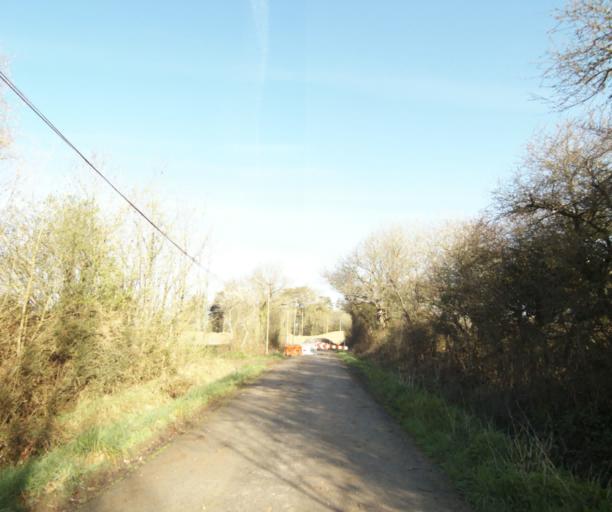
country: FR
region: Pays de la Loire
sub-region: Departement de la Loire-Atlantique
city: Bouvron
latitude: 47.4135
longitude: -1.8349
